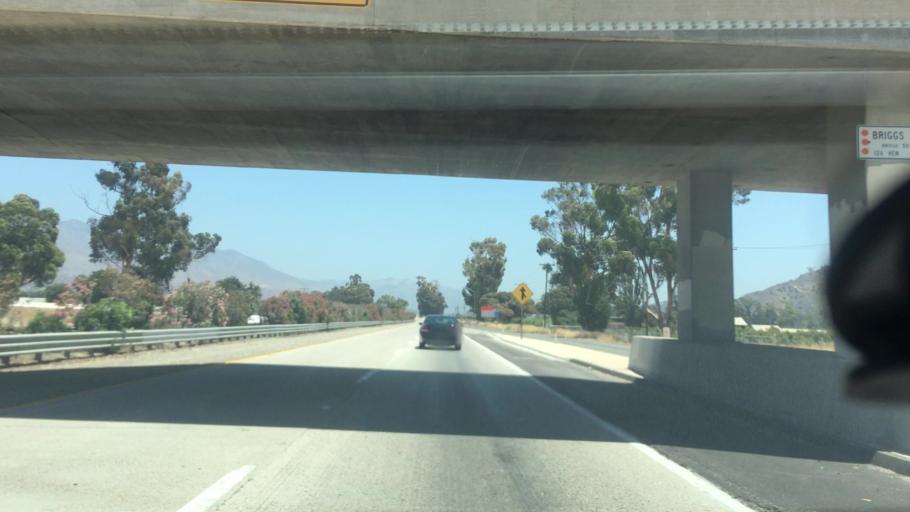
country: US
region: California
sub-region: Ventura County
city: Santa Paula
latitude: 34.3223
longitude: -119.1012
